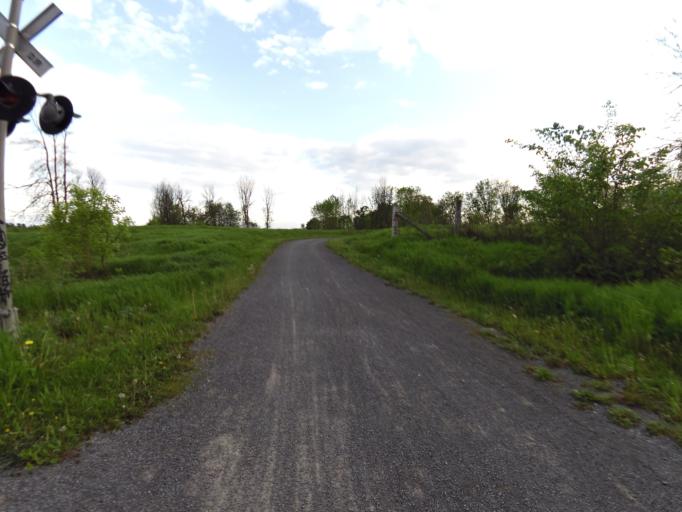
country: CA
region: Ontario
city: Bells Corners
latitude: 45.3318
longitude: -75.8546
